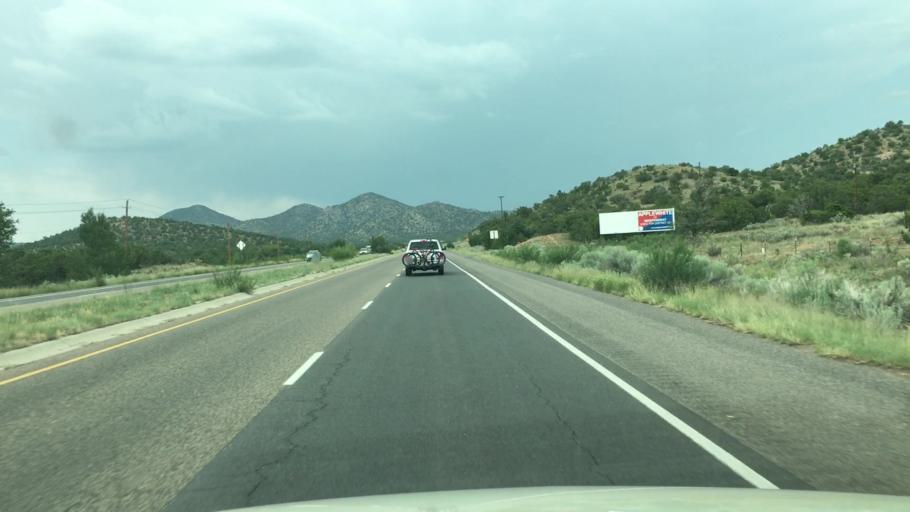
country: US
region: New Mexico
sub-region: Santa Fe County
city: Eldorado at Santa Fe
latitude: 35.5429
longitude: -105.8845
